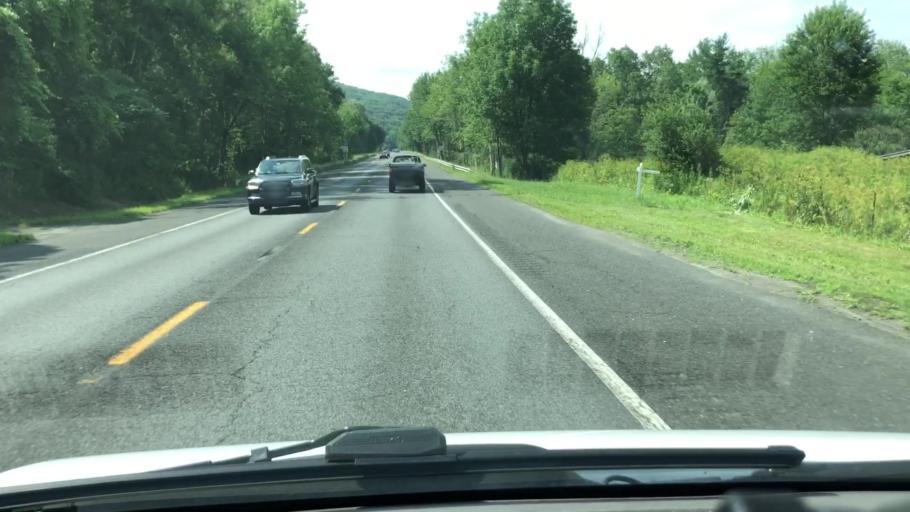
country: US
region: Massachusetts
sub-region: Berkshire County
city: Lanesborough
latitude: 42.5187
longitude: -73.1924
